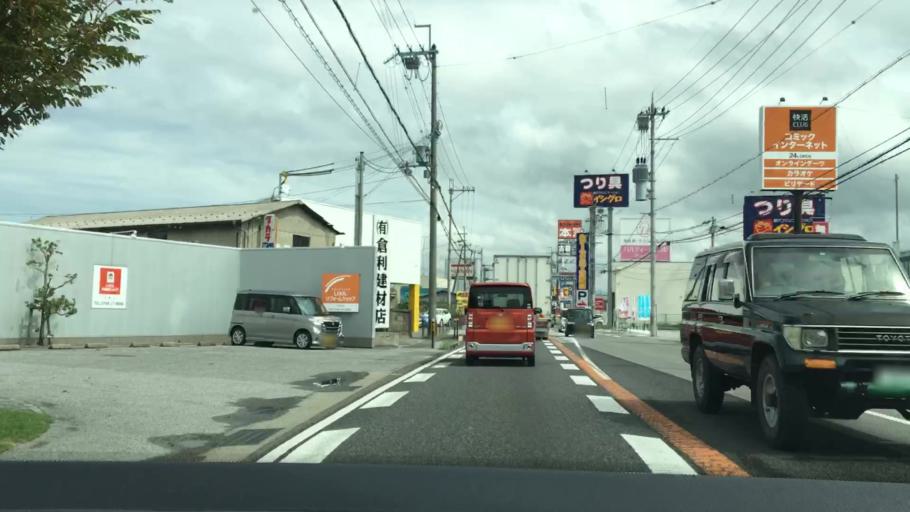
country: JP
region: Shiga Prefecture
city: Hikone
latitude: 35.2418
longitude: 136.2565
